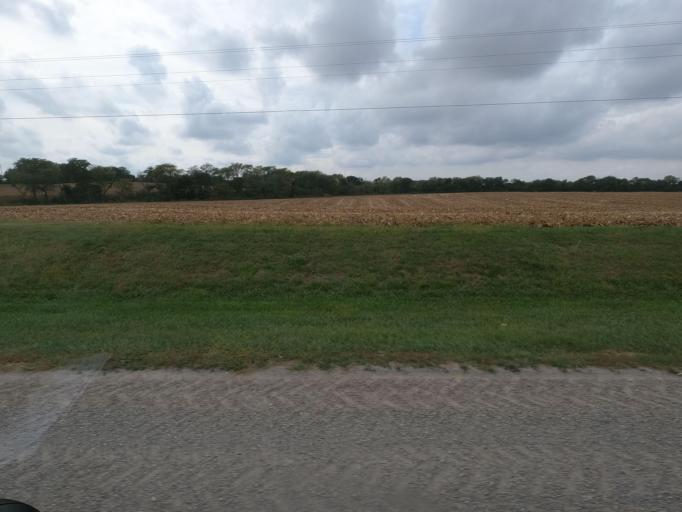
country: US
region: Iowa
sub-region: Wapello County
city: Ottumwa
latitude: 40.9667
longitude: -92.2366
